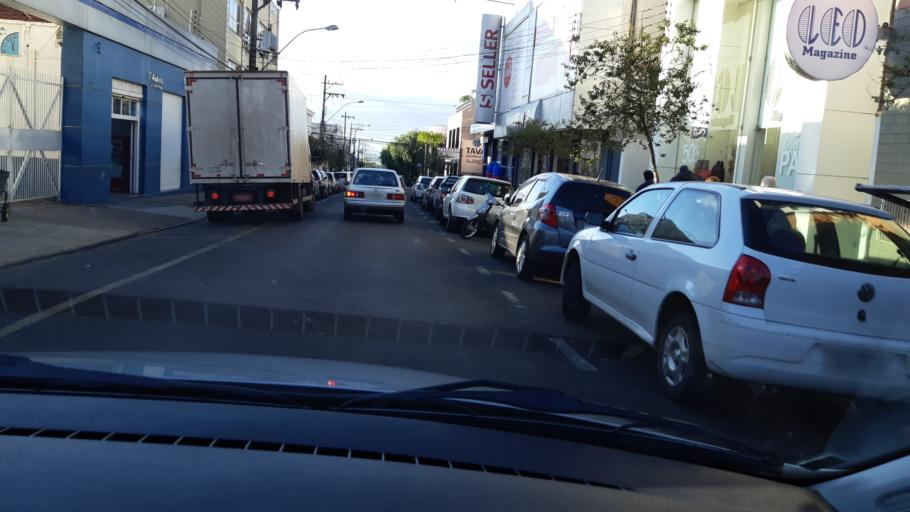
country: BR
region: Sao Paulo
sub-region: Ourinhos
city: Ourinhos
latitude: -22.9788
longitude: -49.8700
